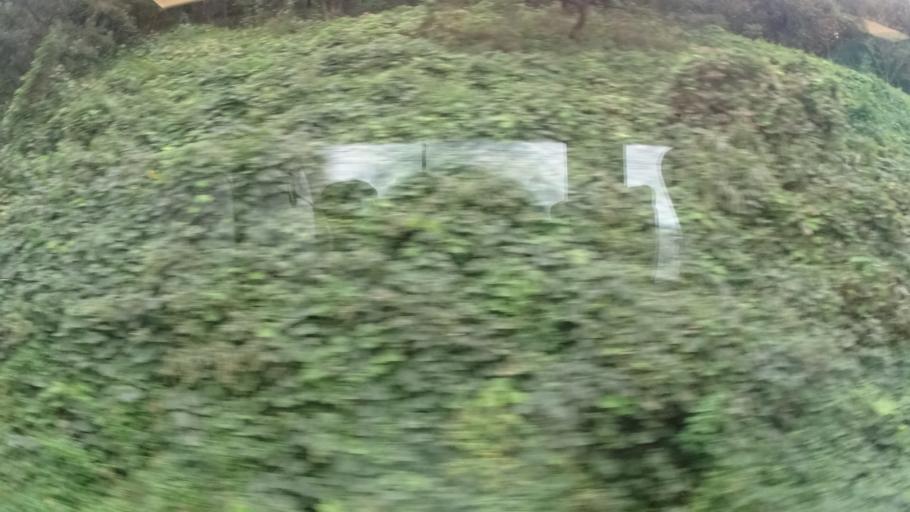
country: JP
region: Yamagata
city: Tsuruoka
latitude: 38.5823
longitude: 139.5604
